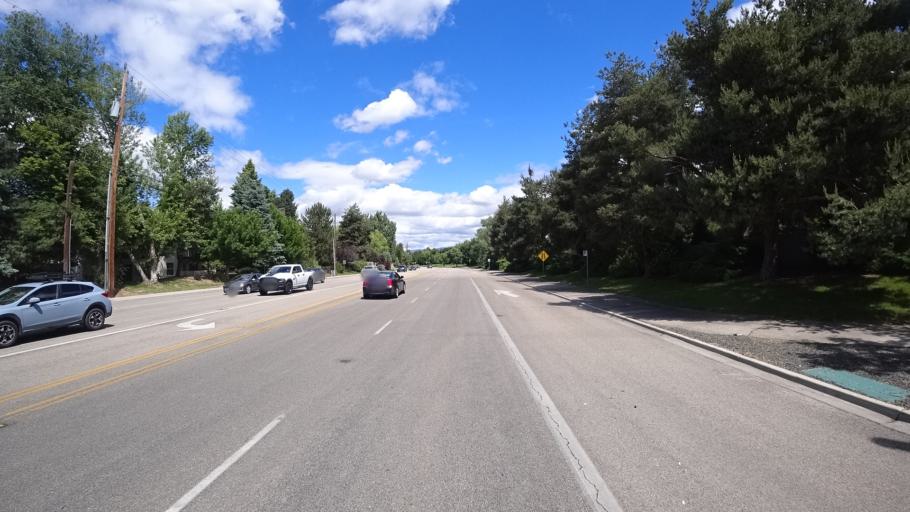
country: US
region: Idaho
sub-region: Ada County
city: Boise
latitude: 43.5861
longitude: -116.1733
